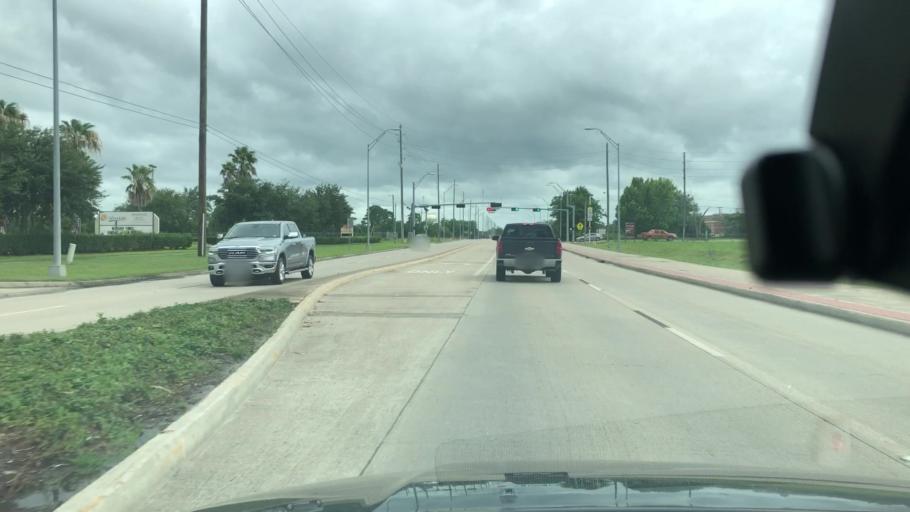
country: US
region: Texas
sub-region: Brazoria County
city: Brookside Village
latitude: 29.5776
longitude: -95.3509
